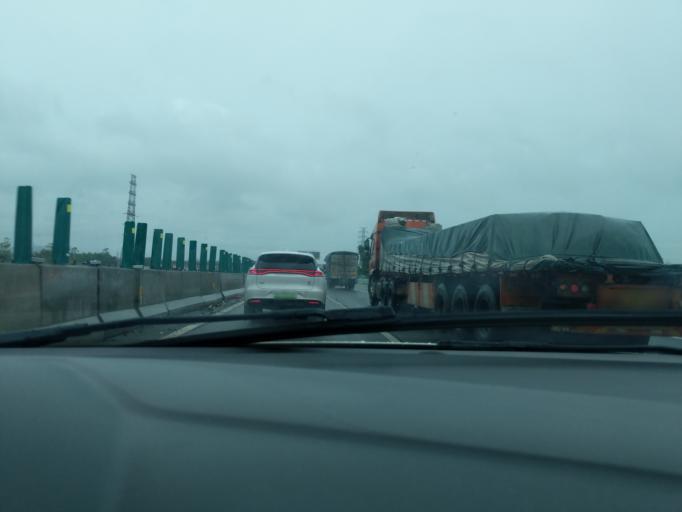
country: CN
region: Guangdong
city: Shuikou
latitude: 22.4694
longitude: 112.7584
